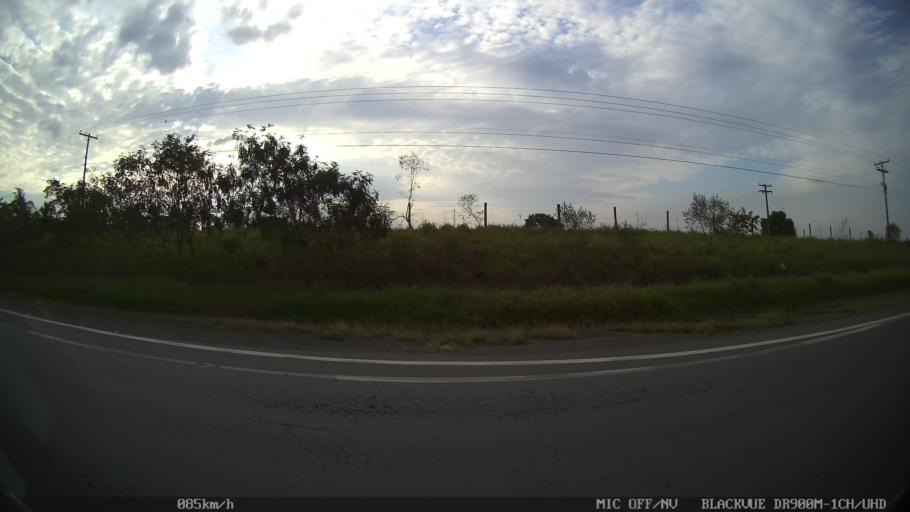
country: BR
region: Sao Paulo
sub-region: Americana
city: Americana
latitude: -22.6354
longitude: -47.3148
